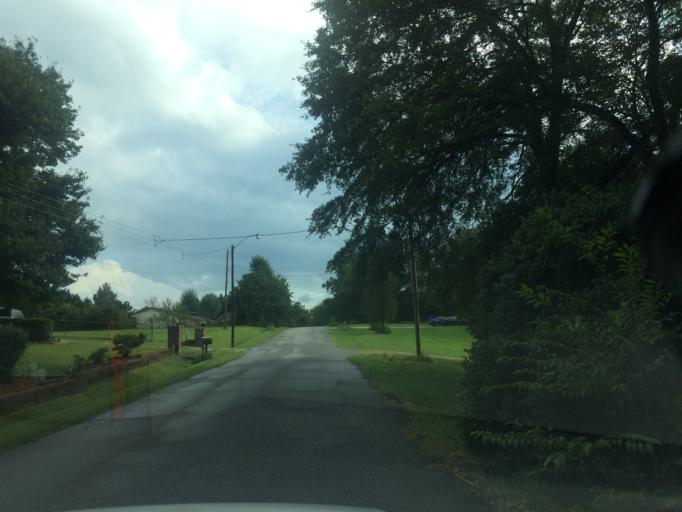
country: US
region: North Carolina
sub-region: Catawba County
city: Conover
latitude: 35.7076
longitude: -81.2649
